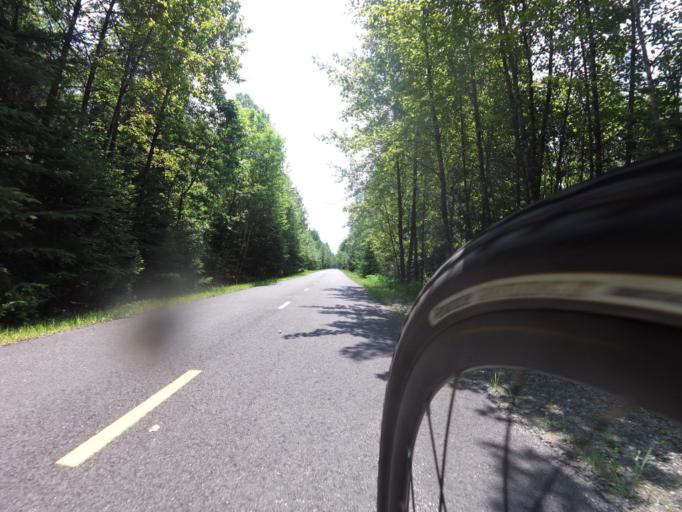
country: CA
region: Quebec
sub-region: Laurentides
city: Mont-Tremblant
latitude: 46.1482
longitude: -74.5938
